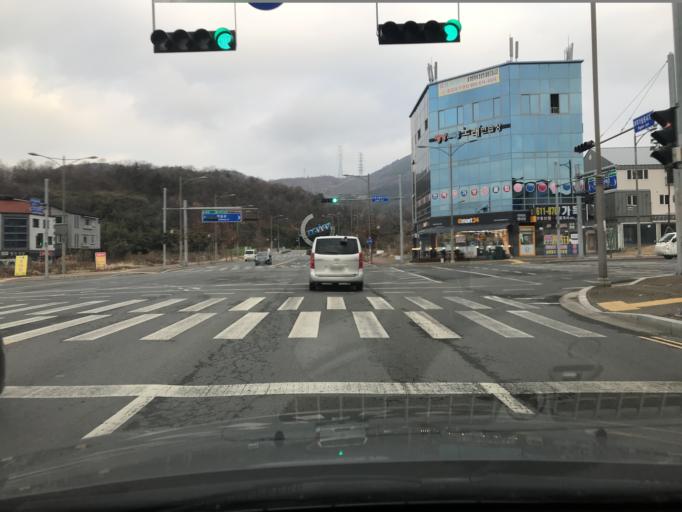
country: KR
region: Daegu
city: Hwawon
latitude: 35.6981
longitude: 128.4578
